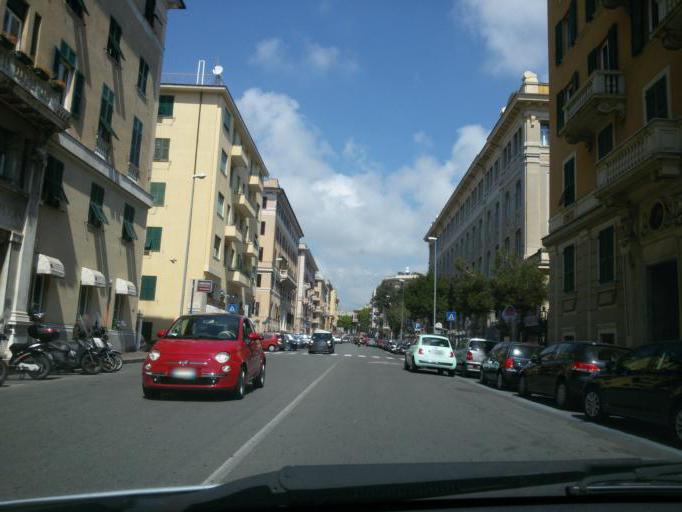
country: IT
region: Liguria
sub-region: Provincia di Genova
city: Genoa
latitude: 44.3989
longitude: 8.9647
